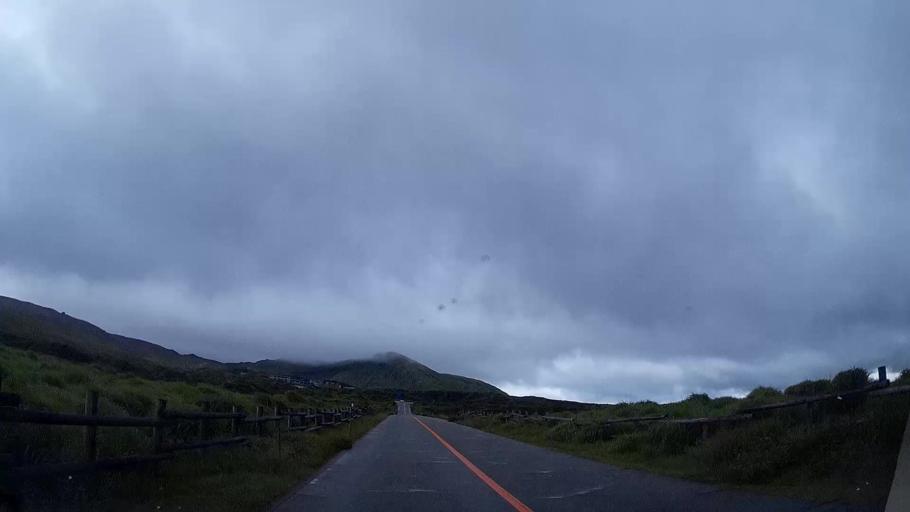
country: JP
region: Kumamoto
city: Aso
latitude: 32.8825
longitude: 131.0676
